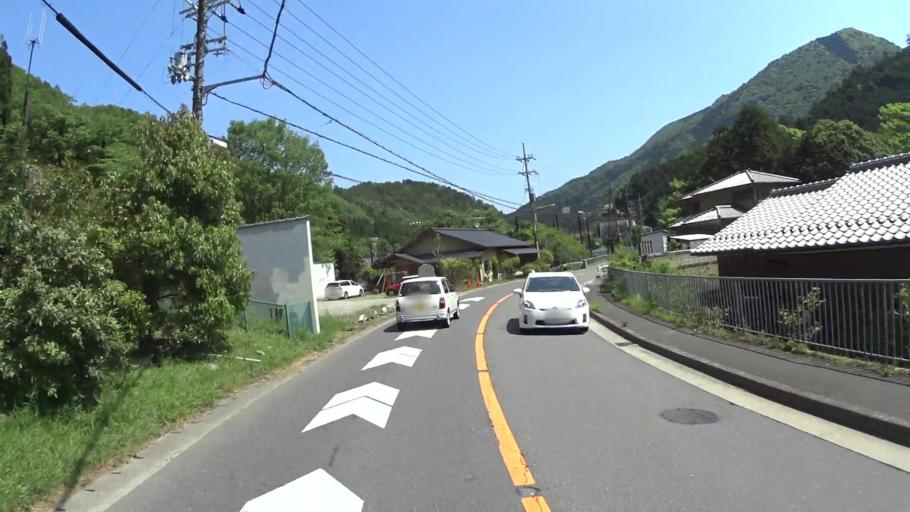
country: JP
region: Kyoto
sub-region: Kyoto-shi
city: Kamigyo-ku
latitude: 35.0828
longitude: 135.8169
